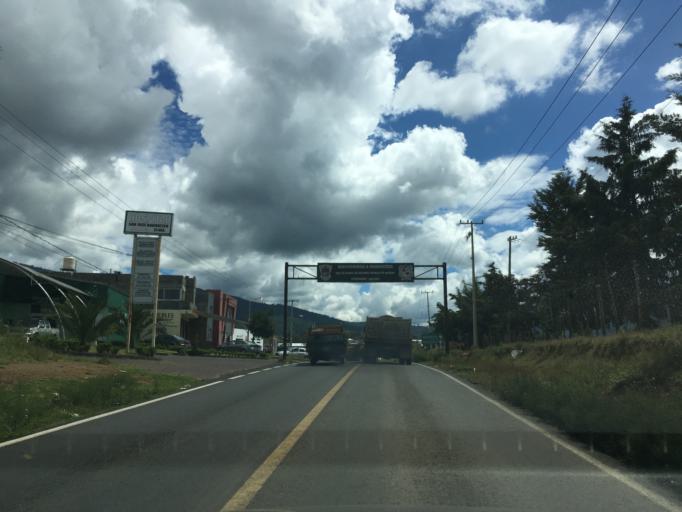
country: MX
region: Michoacan
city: Nahuatzen
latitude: 19.6578
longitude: -101.9282
